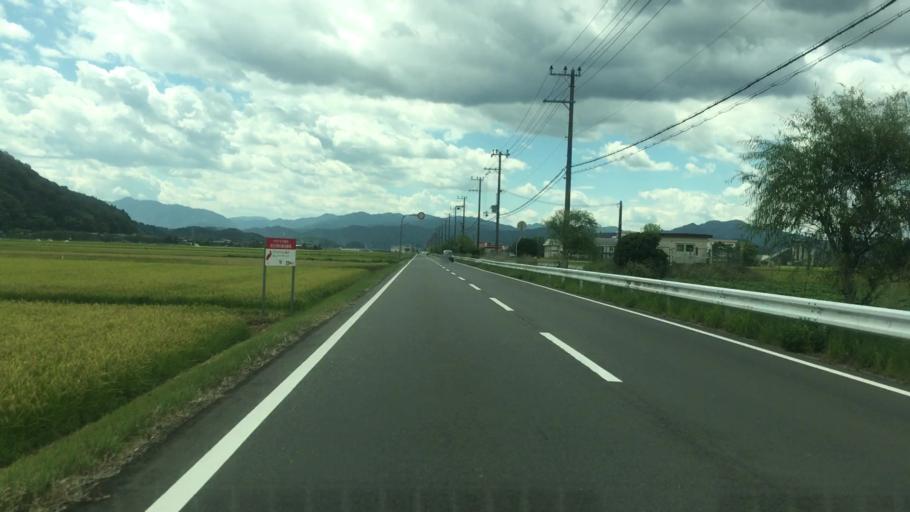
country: JP
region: Hyogo
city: Toyooka
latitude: 35.5347
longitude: 134.8397
